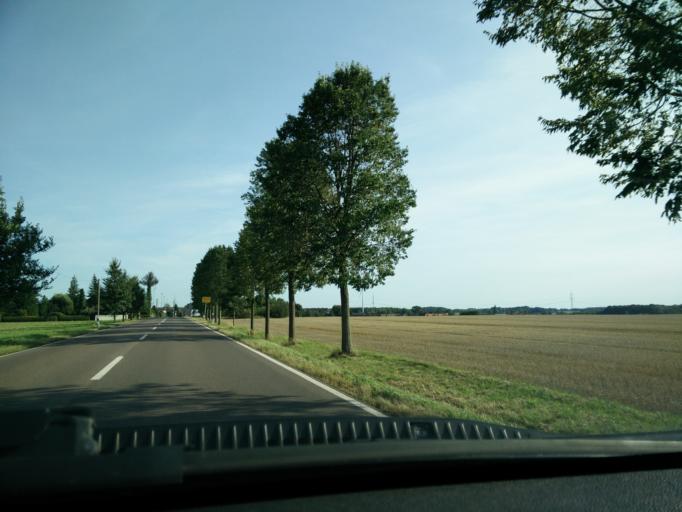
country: DE
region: Saxony
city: Geithain
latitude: 51.1066
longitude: 12.6919
